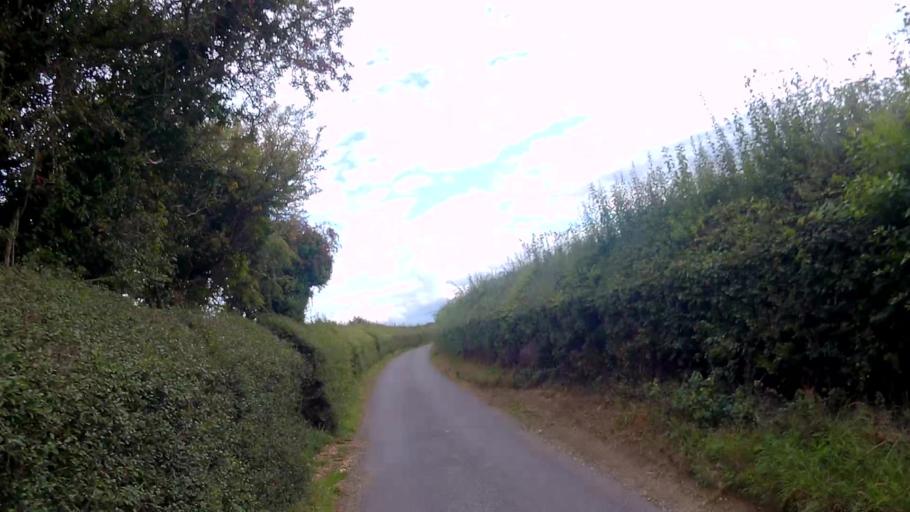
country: GB
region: England
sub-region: Hampshire
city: Kings Worthy
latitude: 51.1626
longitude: -1.3289
